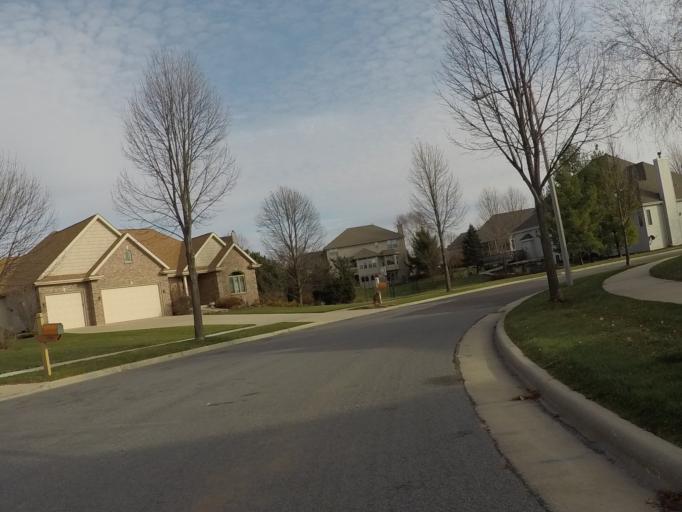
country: US
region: Wisconsin
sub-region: Dane County
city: Middleton
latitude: 43.0805
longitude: -89.5519
